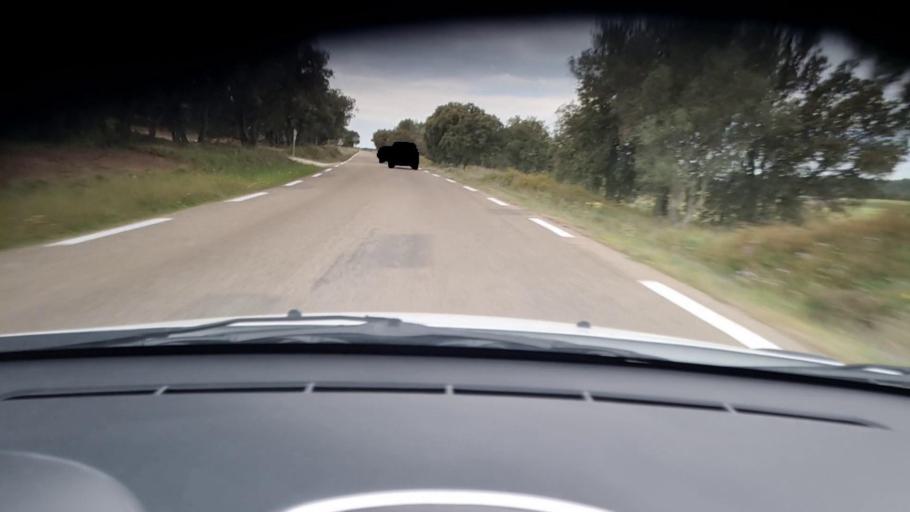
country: FR
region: Languedoc-Roussillon
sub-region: Departement du Gard
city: Blauzac
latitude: 43.9744
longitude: 4.3989
